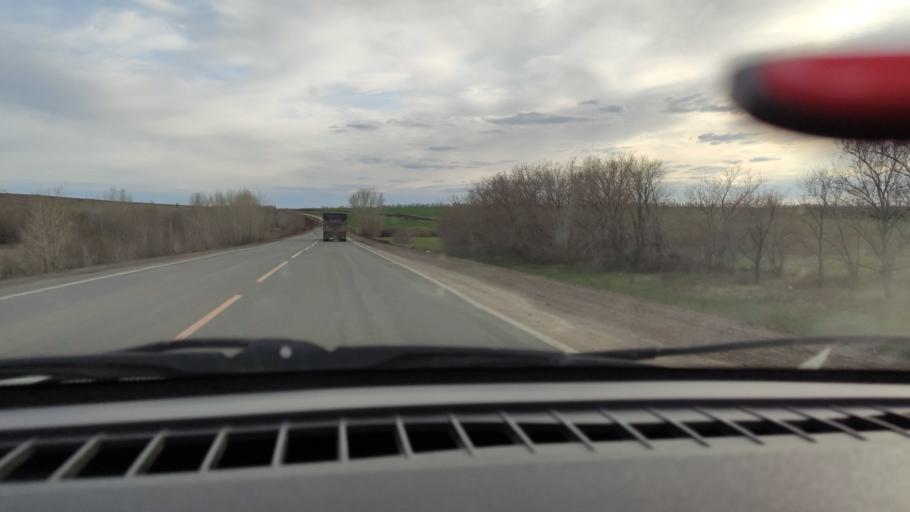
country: RU
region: Orenburg
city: Sakmara
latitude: 52.1911
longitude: 55.3013
